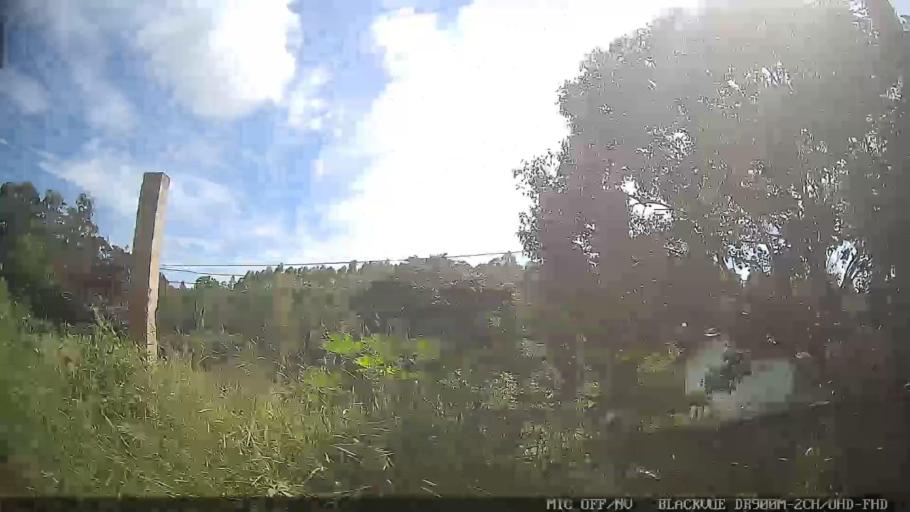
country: BR
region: Sao Paulo
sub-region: Jarinu
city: Jarinu
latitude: -23.0106
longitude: -46.6524
